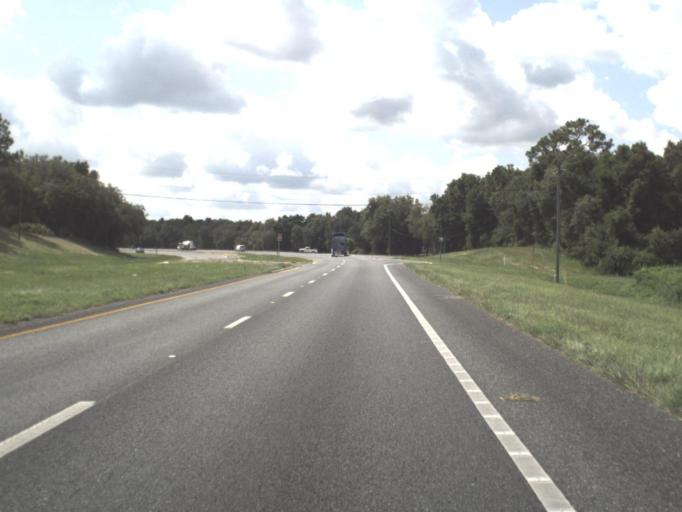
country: US
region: Florida
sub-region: Hernando County
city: Ridge Manor
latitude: 28.5121
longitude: -82.2041
